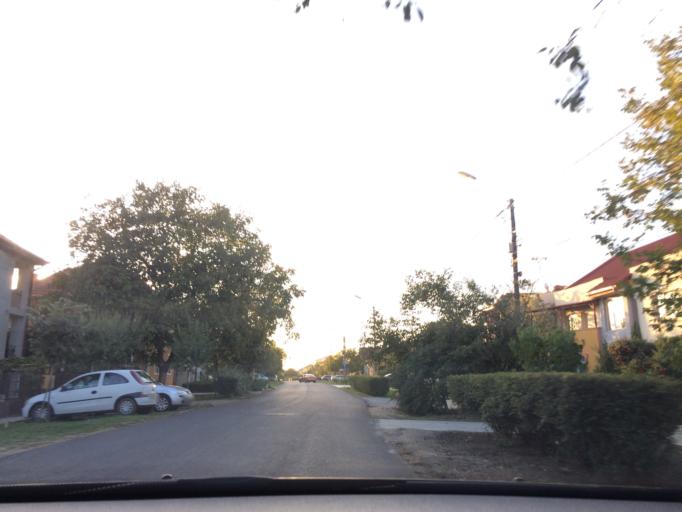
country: RO
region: Timis
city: Timisoara
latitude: 45.7628
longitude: 21.1938
